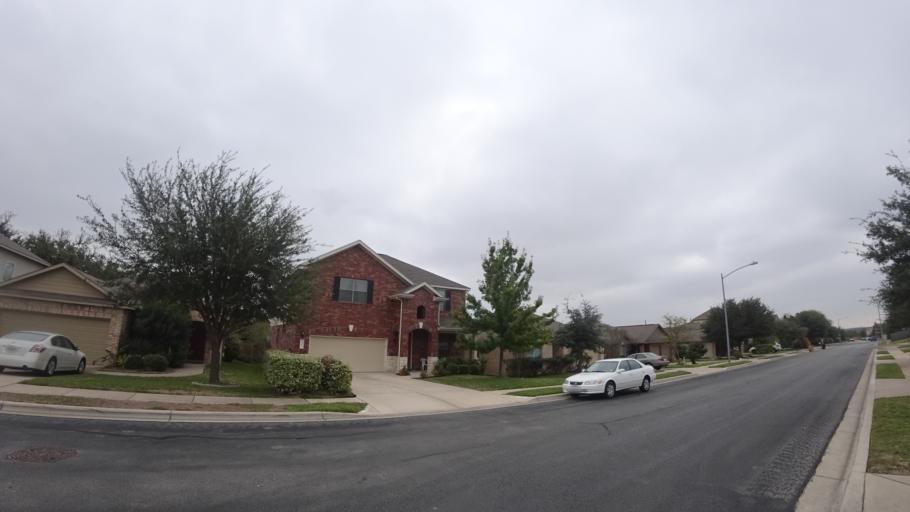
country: US
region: Texas
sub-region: Travis County
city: Pflugerville
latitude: 30.3738
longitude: -97.6479
